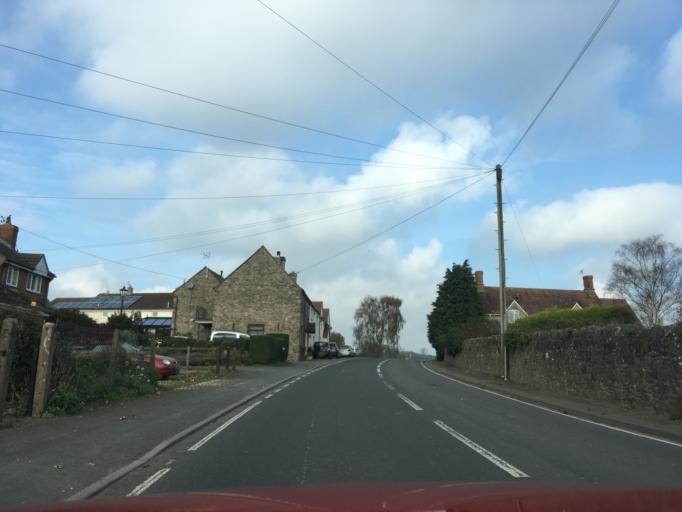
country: GB
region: England
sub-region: South Gloucestershire
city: Falfield
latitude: 51.6123
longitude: -2.4396
